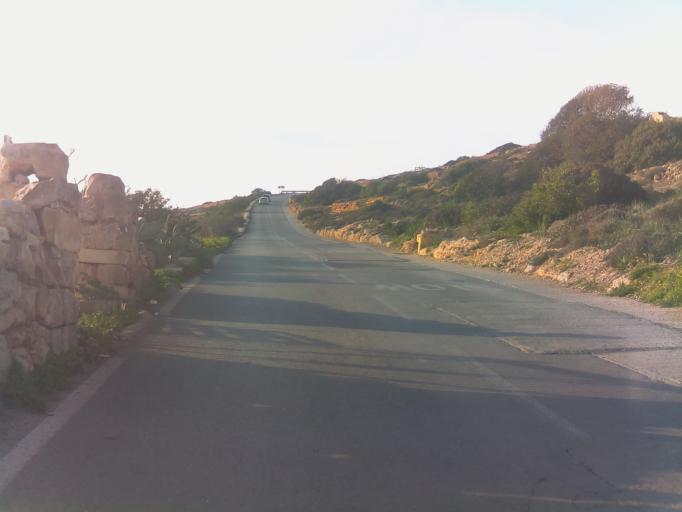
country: MT
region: Il-Mellieha
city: Mellieha
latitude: 35.9483
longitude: 14.3515
